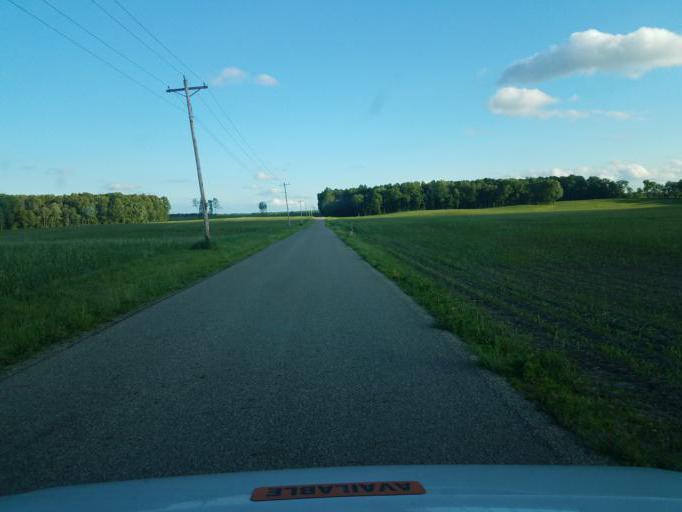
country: US
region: Ohio
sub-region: Knox County
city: Fredericktown
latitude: 40.4531
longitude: -82.6253
